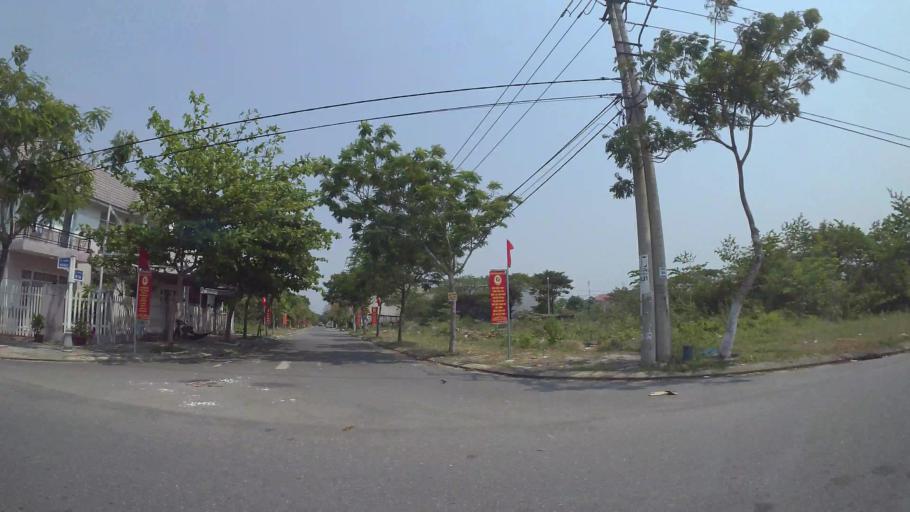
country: VN
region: Da Nang
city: Cam Le
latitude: 15.9992
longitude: 108.2026
